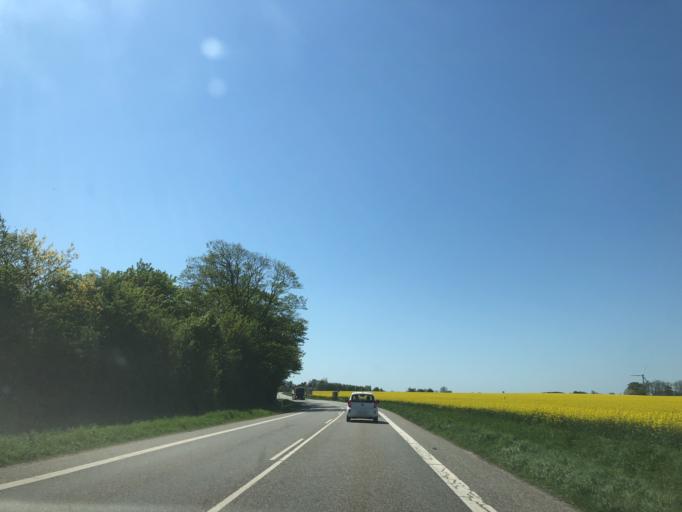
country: DK
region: Zealand
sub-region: Slagelse Kommune
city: Forlev
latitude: 55.3539
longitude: 11.2431
